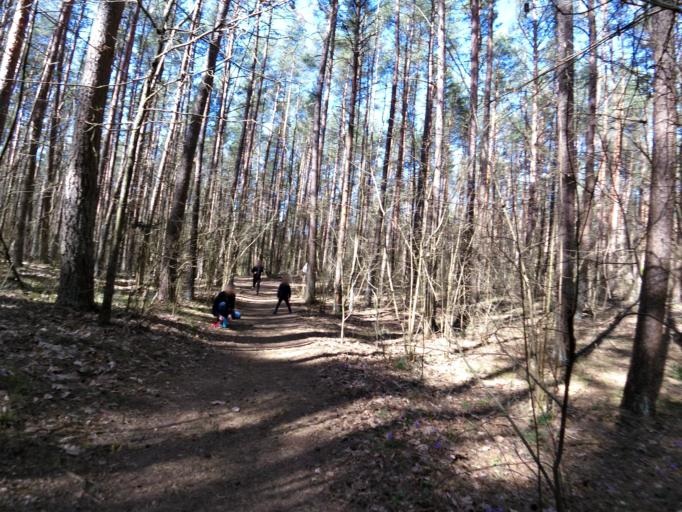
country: LT
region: Vilnius County
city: Pilaite
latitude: 54.6949
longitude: 25.1935
